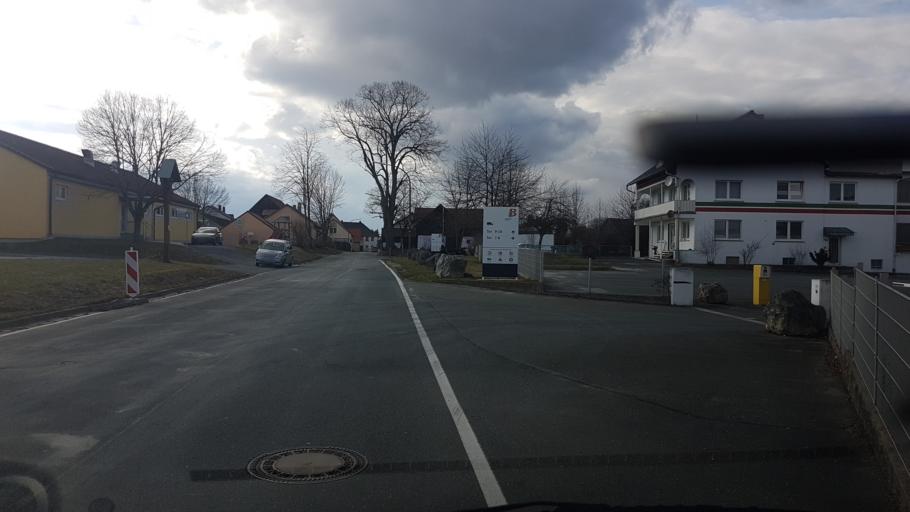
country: DE
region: Bavaria
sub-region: Upper Franconia
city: Stadelhofen
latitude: 50.0012
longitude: 11.2010
